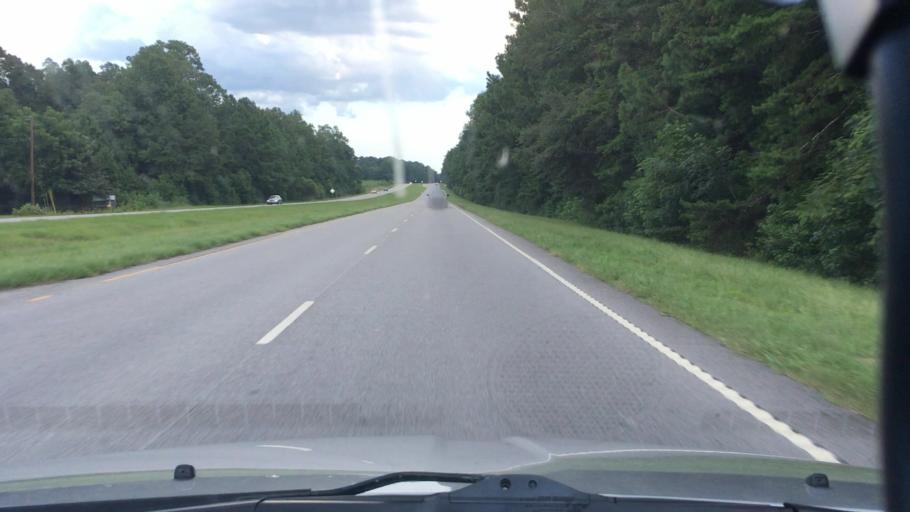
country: US
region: South Carolina
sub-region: Hampton County
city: Yemassee
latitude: 32.6331
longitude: -80.8387
